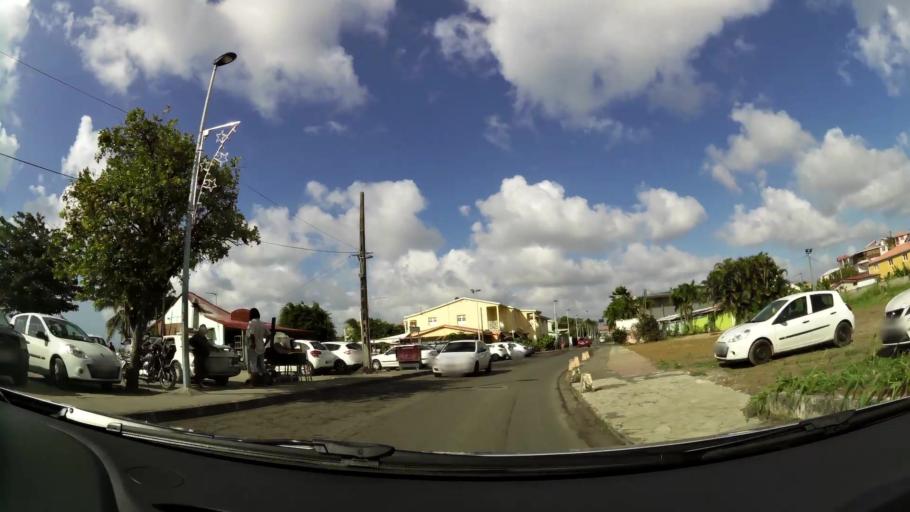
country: MQ
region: Martinique
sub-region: Martinique
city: Les Trois-Ilets
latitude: 14.5525
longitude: -61.0529
